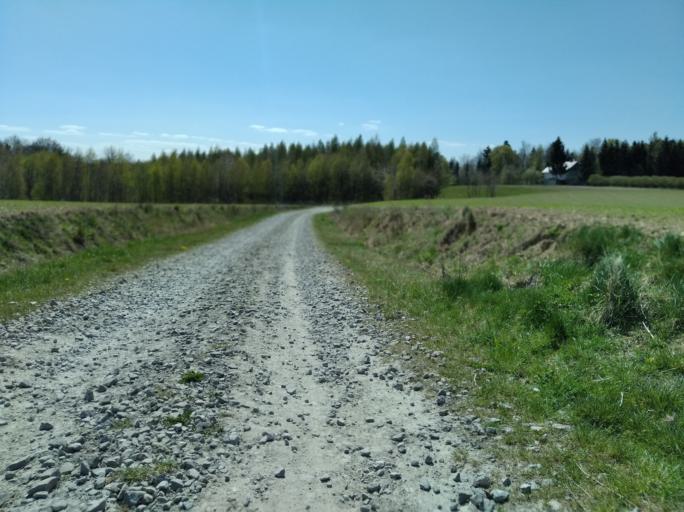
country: PL
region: Subcarpathian Voivodeship
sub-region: Powiat strzyzowski
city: Wisniowa
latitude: 49.9039
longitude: 21.7112
